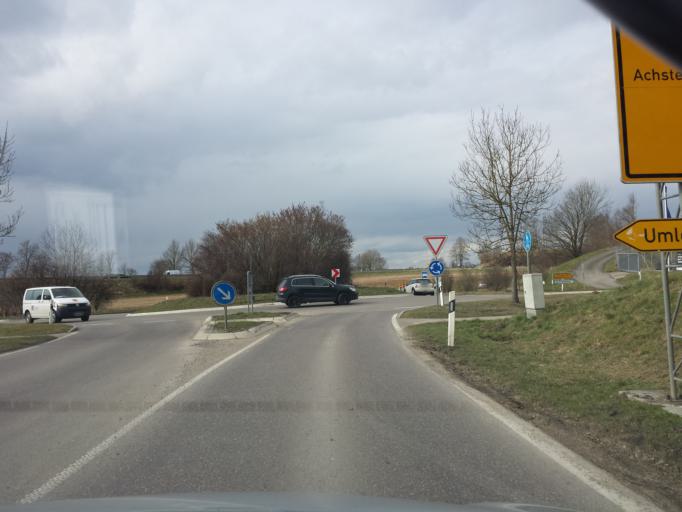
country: DE
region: Baden-Wuerttemberg
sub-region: Tuebingen Region
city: Achstetten
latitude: 48.2591
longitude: 9.9081
